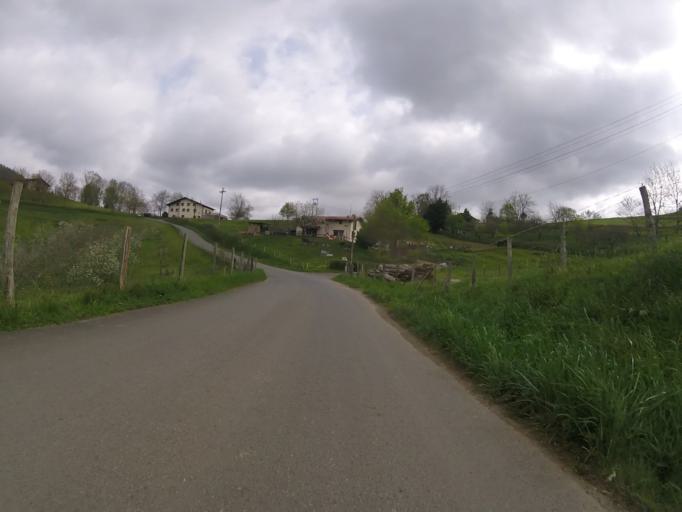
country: ES
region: Basque Country
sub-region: Provincia de Guipuzcoa
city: Zizurkil
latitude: 43.2063
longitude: -2.0748
